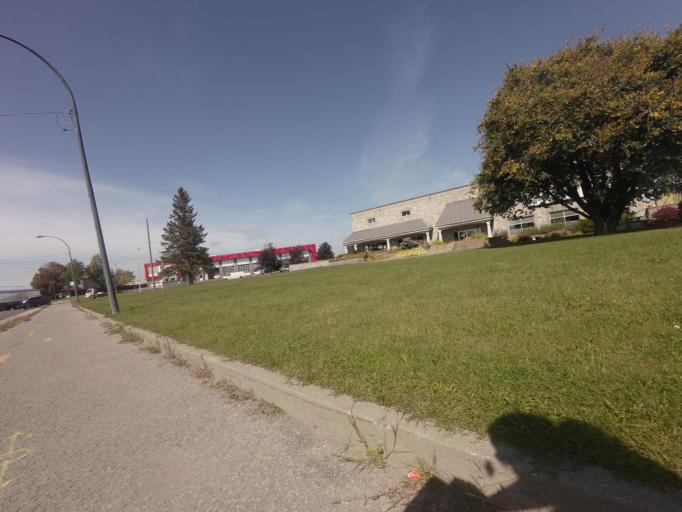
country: CA
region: Quebec
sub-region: Laurentides
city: Saint-Eustache
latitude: 45.5653
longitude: -73.9211
